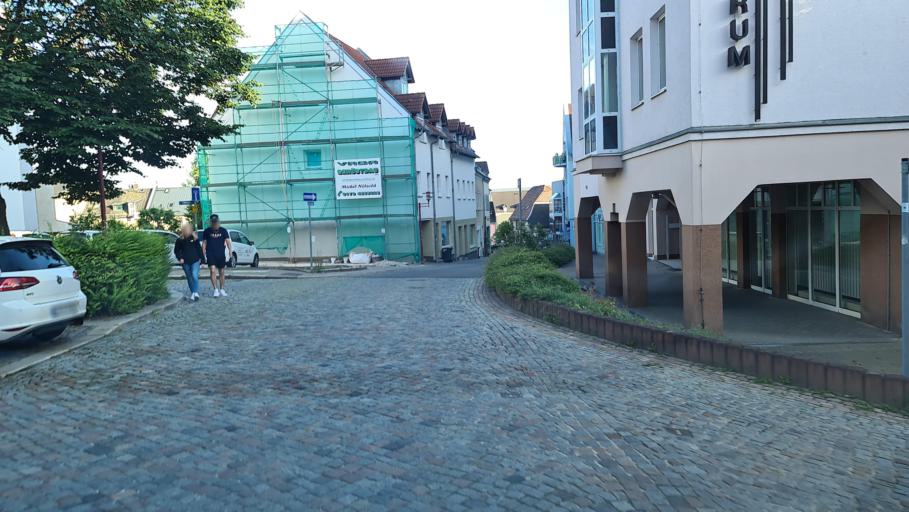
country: DE
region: Saxony
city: Hohenstein-Ernstthal
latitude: 50.8004
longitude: 12.7105
